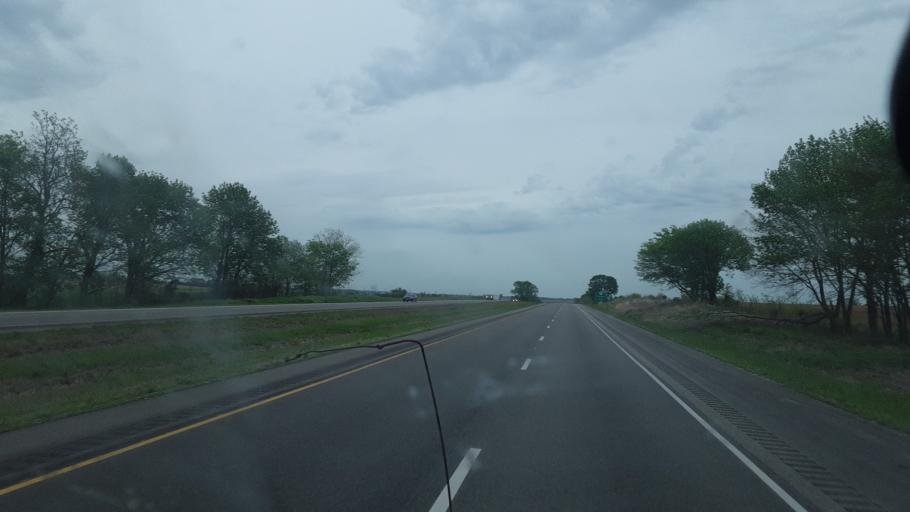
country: US
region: Indiana
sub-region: Posey County
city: Poseyville
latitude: 38.1842
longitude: -87.8017
